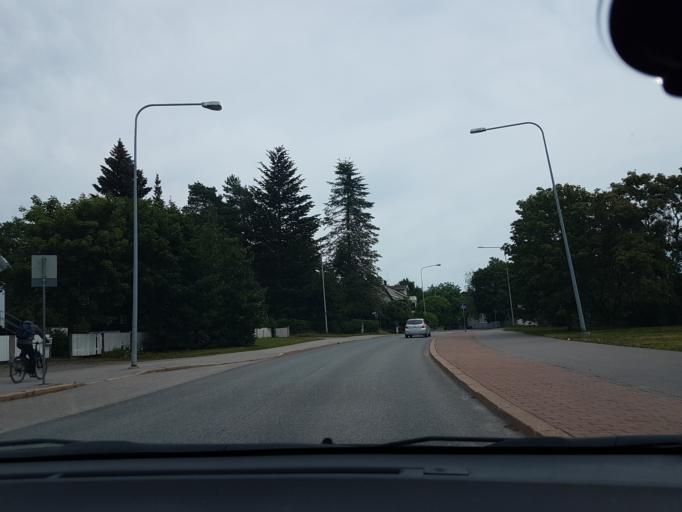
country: FI
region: Uusimaa
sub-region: Helsinki
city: Vantaa
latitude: 60.2617
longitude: 25.0053
